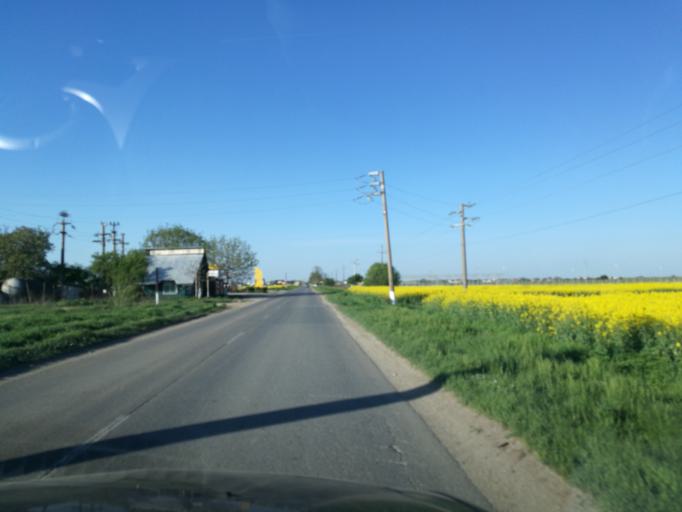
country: RO
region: Ilfov
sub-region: Comuna Vidra
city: Vidra
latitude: 44.2829
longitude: 26.1804
